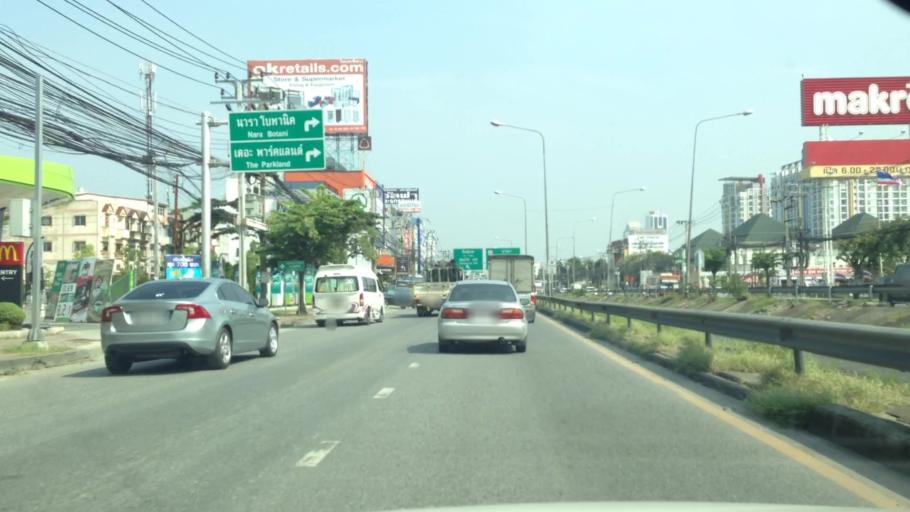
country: TH
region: Bangkok
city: Bang Na
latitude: 13.6500
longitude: 100.6400
